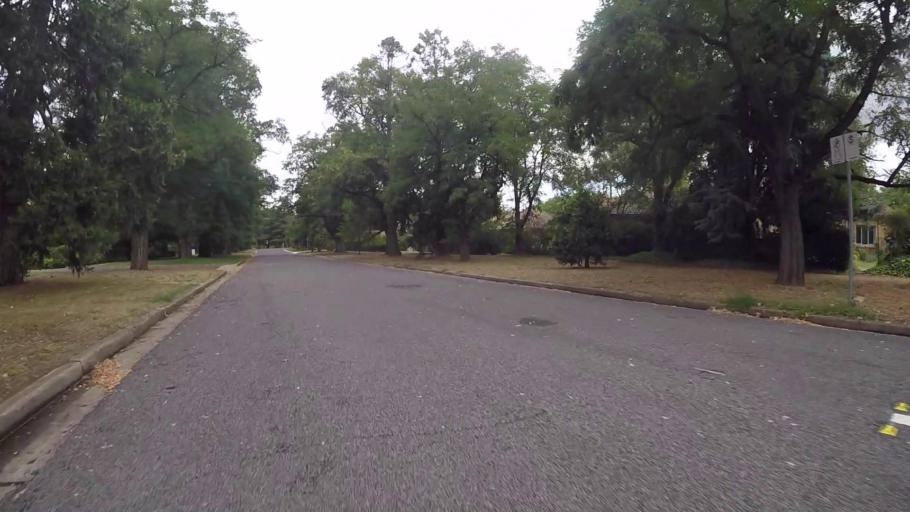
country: AU
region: Australian Capital Territory
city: Forrest
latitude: -35.3125
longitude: 149.1367
